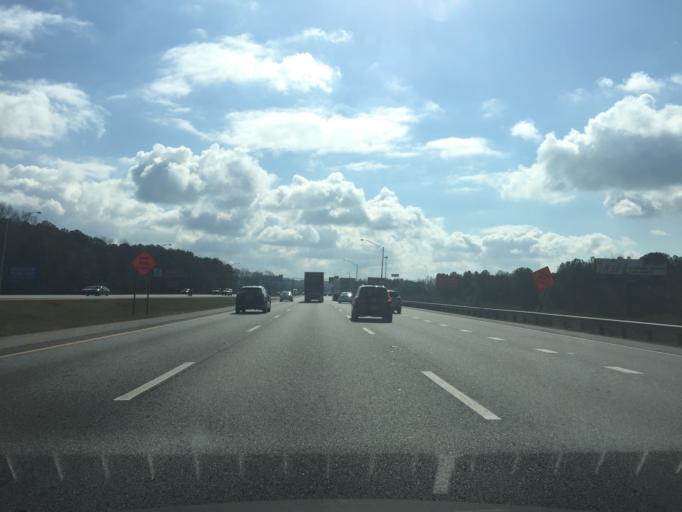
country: US
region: Tennessee
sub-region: Hamilton County
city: East Ridge
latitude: 35.0000
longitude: -85.2108
